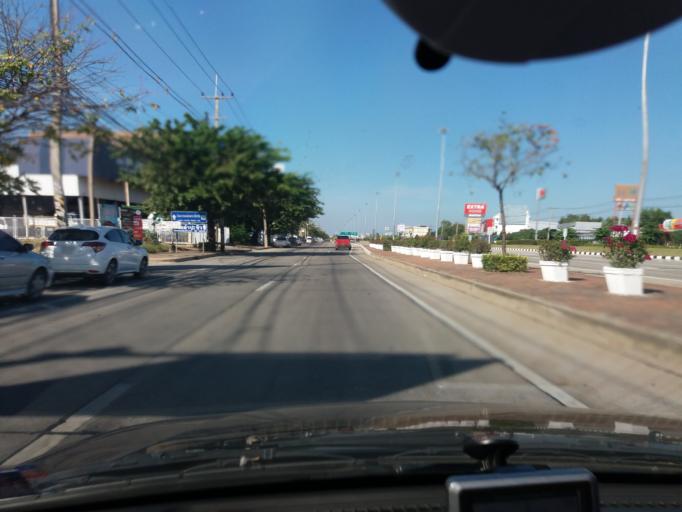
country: TH
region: Suphan Buri
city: Suphan Buri
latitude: 14.4807
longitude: 100.1313
